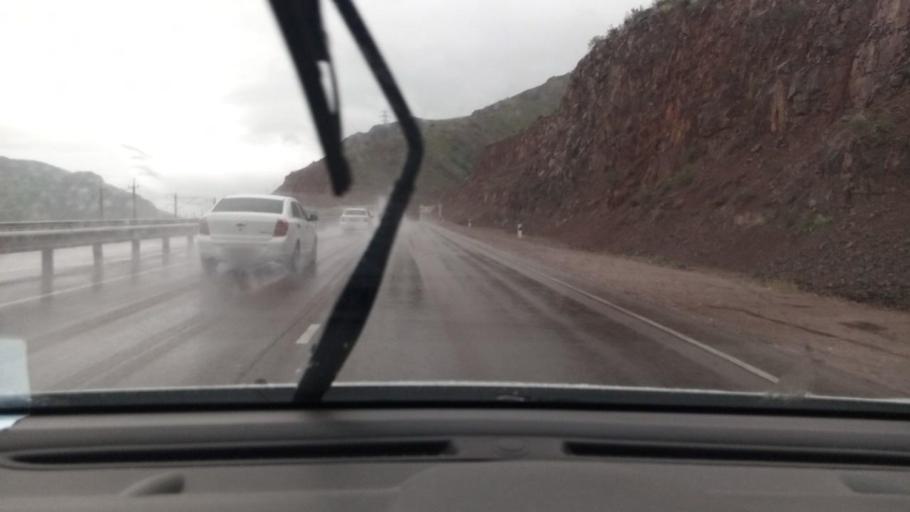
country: UZ
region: Toshkent
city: Angren
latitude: 41.0768
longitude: 70.3006
